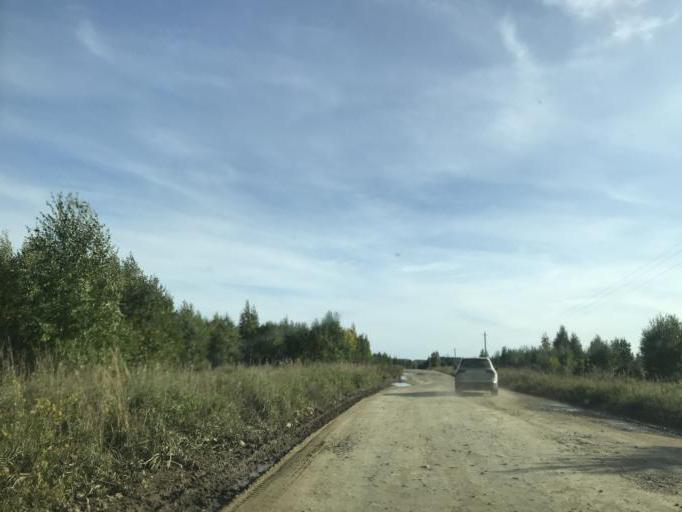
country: RU
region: Chelyabinsk
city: Poletayevo
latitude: 54.9761
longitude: 60.9699
